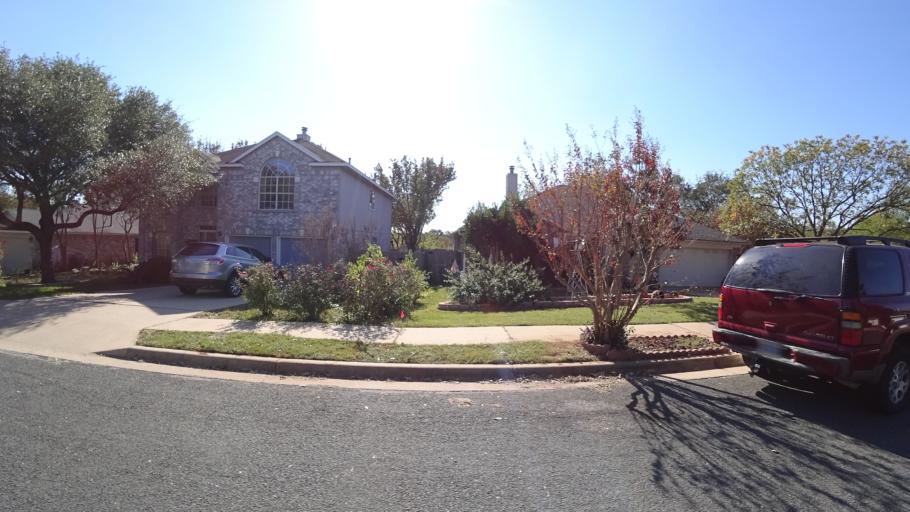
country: US
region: Texas
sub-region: Travis County
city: Shady Hollow
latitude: 30.2187
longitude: -97.8626
